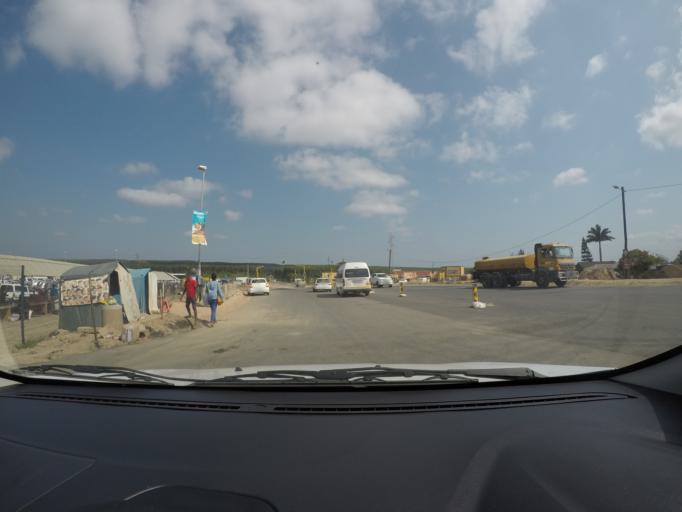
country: ZA
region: KwaZulu-Natal
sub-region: uThungulu District Municipality
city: eSikhawini
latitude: -28.8719
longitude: 31.9010
